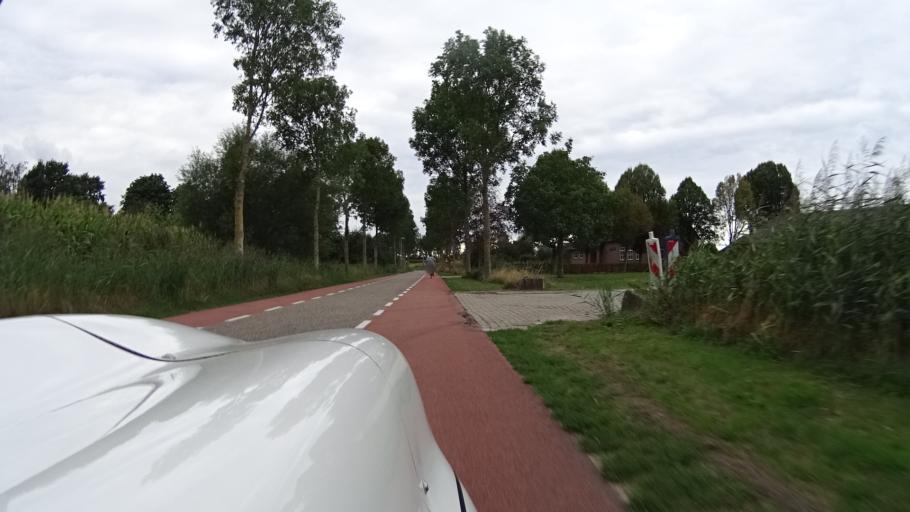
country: NL
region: North Brabant
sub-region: Gemeente Veghel
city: Mariaheide
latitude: 51.6514
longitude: 5.5755
